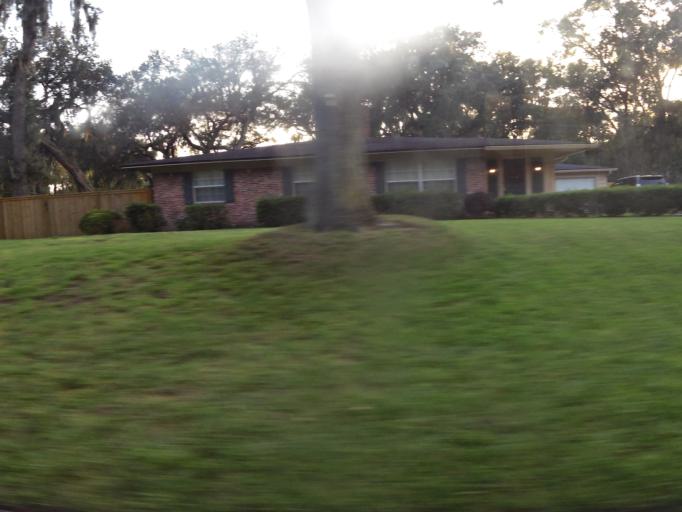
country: US
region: Florida
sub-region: Duval County
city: Jacksonville
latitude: 30.2654
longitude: -81.7120
